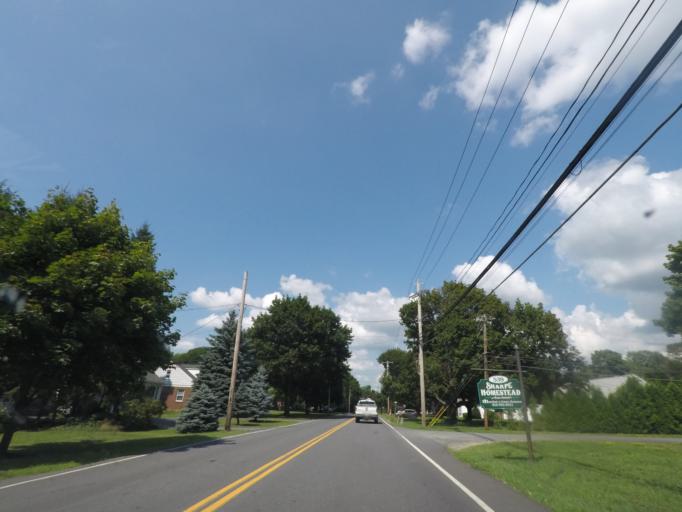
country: US
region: New York
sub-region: Albany County
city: Menands
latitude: 42.6609
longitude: -73.6898
